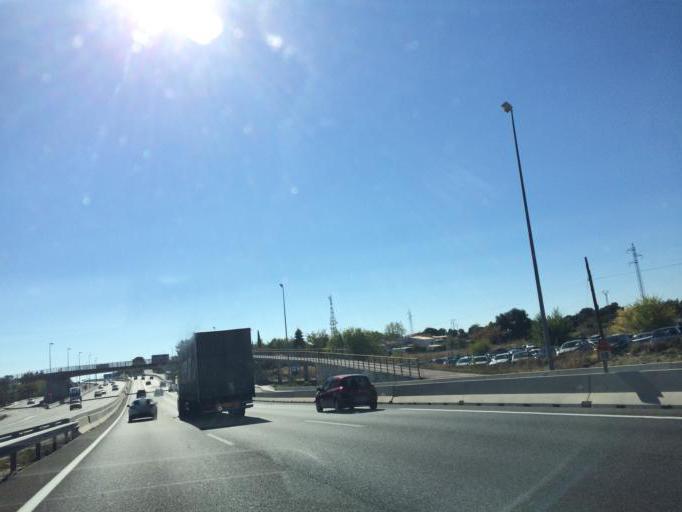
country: ES
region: Madrid
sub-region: Provincia de Madrid
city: Tres Cantos
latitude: 40.5566
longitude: -3.7109
